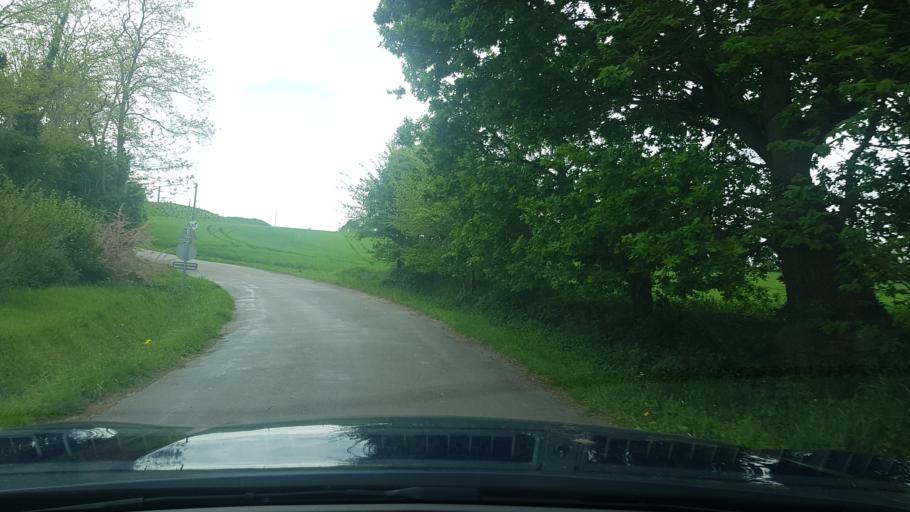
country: FR
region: Brittany
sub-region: Departement du Morbihan
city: Ploemeur
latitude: 47.7507
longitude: -3.4148
